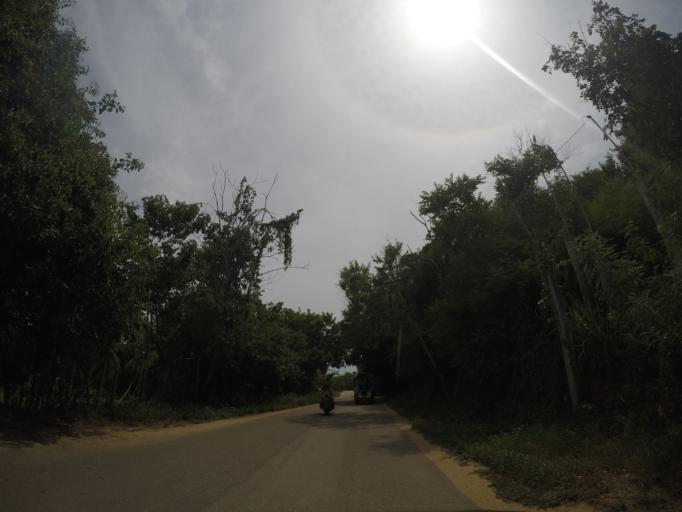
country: MX
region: Oaxaca
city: Santa Maria Tonameca
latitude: 15.6671
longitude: -96.5402
